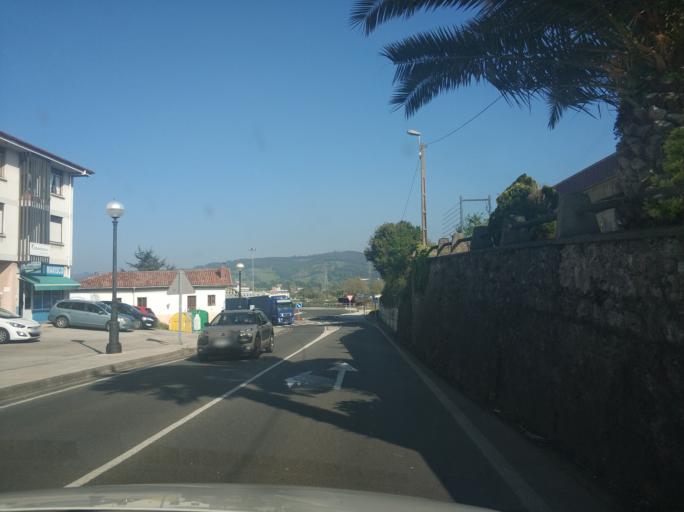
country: ES
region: Cantabria
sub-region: Provincia de Cantabria
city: Colindres
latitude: 43.3932
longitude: -3.4679
